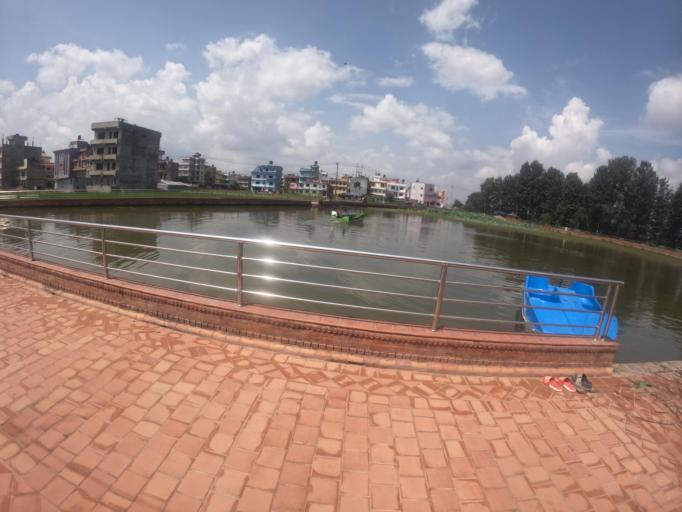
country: NP
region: Central Region
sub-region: Bagmati Zone
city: Bhaktapur
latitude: 27.6912
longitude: 85.3867
